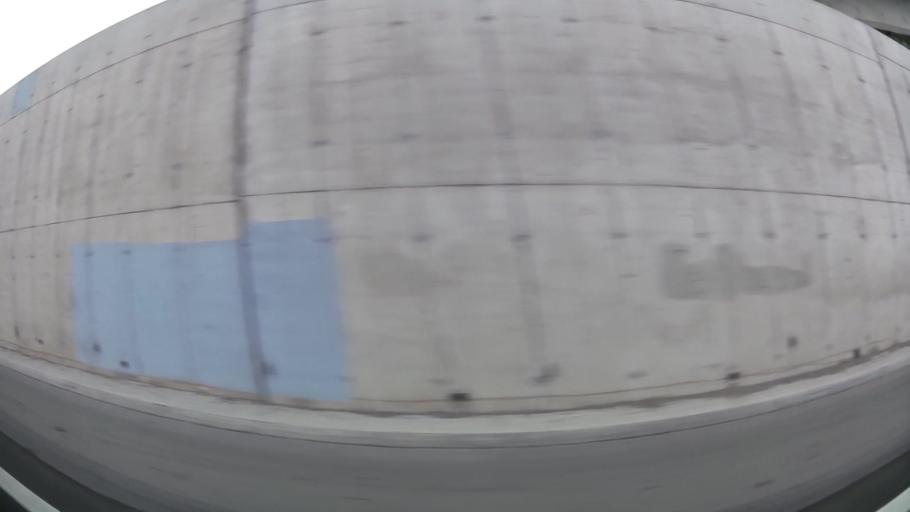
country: CL
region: Santiago Metropolitan
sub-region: Provincia de Santiago
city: Lo Prado
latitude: -33.4169
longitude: -70.6914
